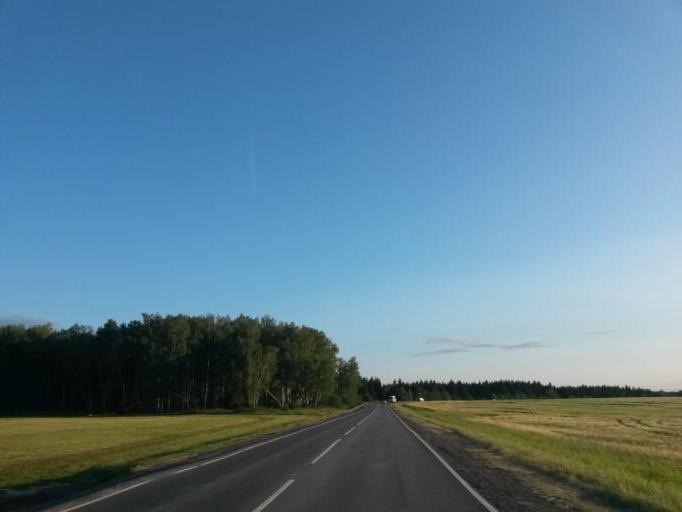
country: RU
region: Moskovskaya
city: Vostryakovo
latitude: 55.3557
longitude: 37.7665
